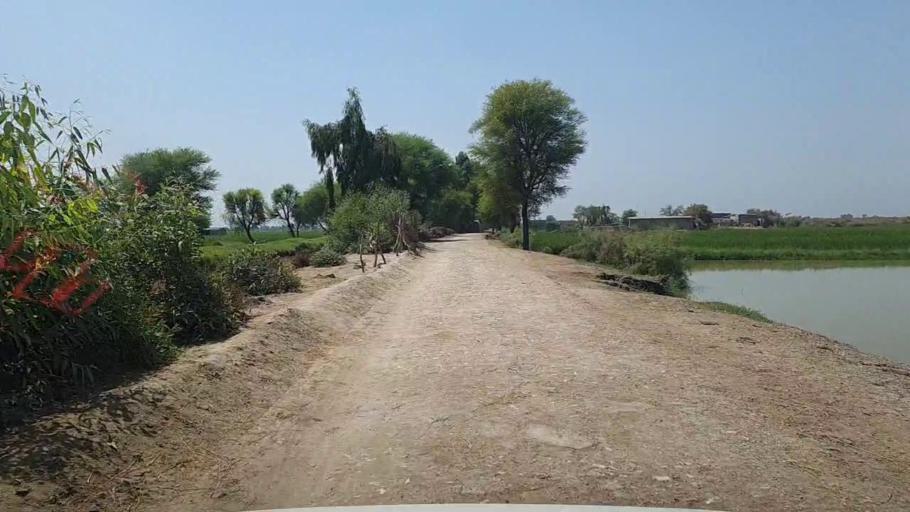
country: PK
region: Sindh
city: Kandhkot
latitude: 28.3433
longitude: 69.3093
